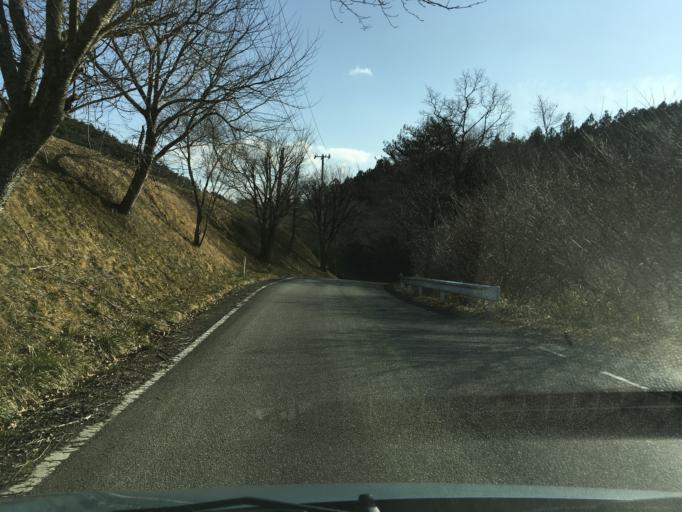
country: JP
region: Iwate
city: Ichinoseki
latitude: 38.7963
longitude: 141.4481
